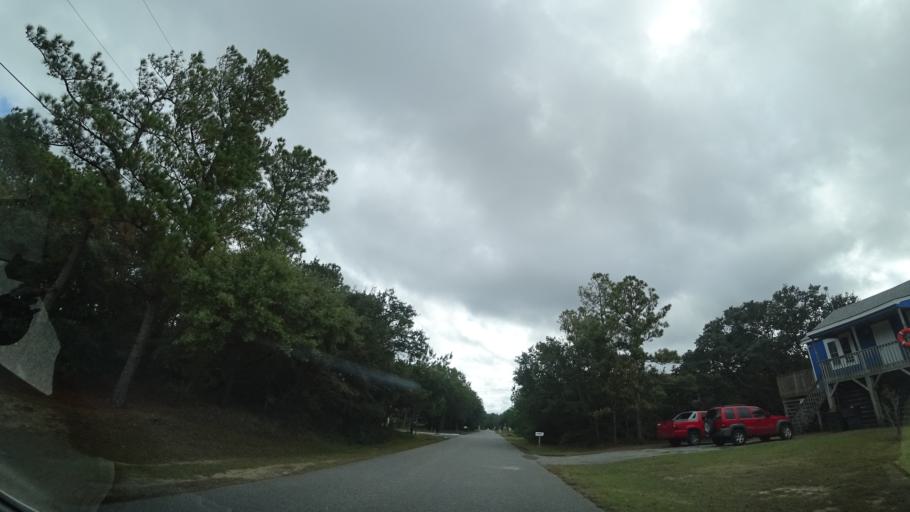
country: US
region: North Carolina
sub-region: Dare County
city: Kill Devil Hills
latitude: 36.0044
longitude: -75.6603
